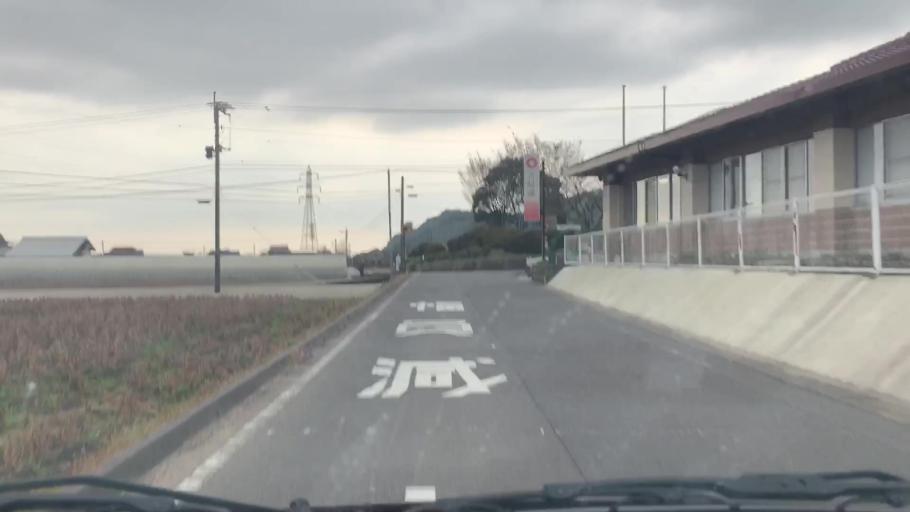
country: JP
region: Saga Prefecture
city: Kashima
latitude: 33.1228
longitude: 130.0573
